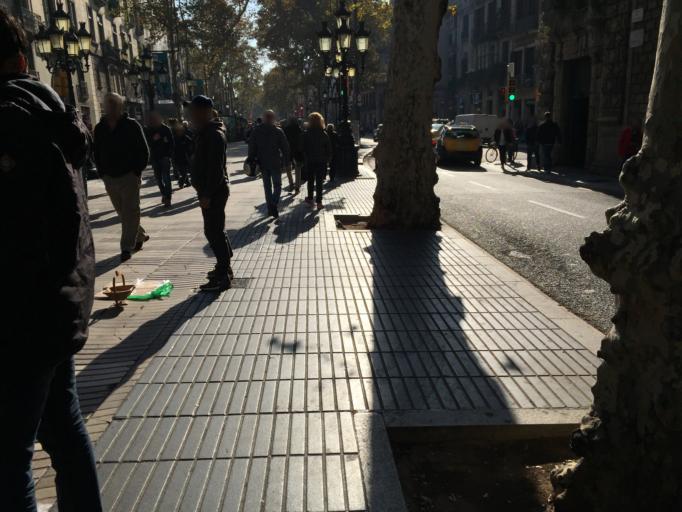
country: ES
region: Catalonia
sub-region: Provincia de Barcelona
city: Ciutat Vella
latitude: 41.3832
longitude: 2.1713
